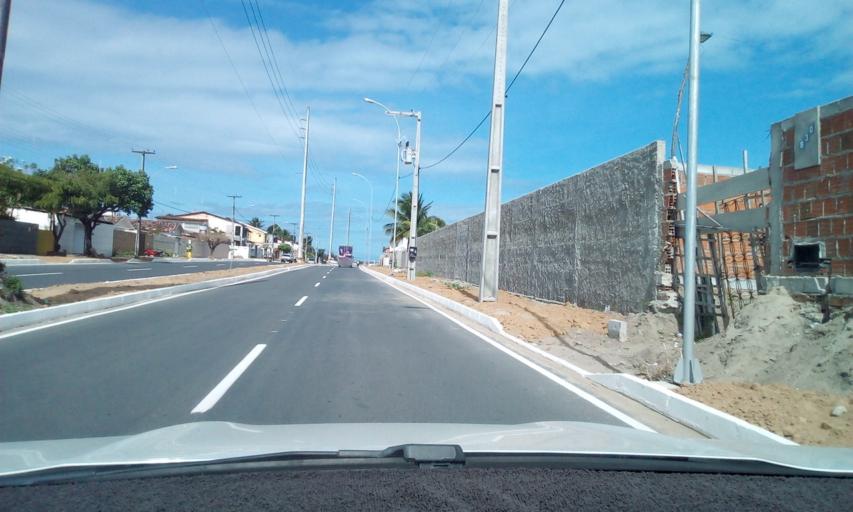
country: BR
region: Paraiba
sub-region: Conde
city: Conde
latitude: -7.2083
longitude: -34.8444
